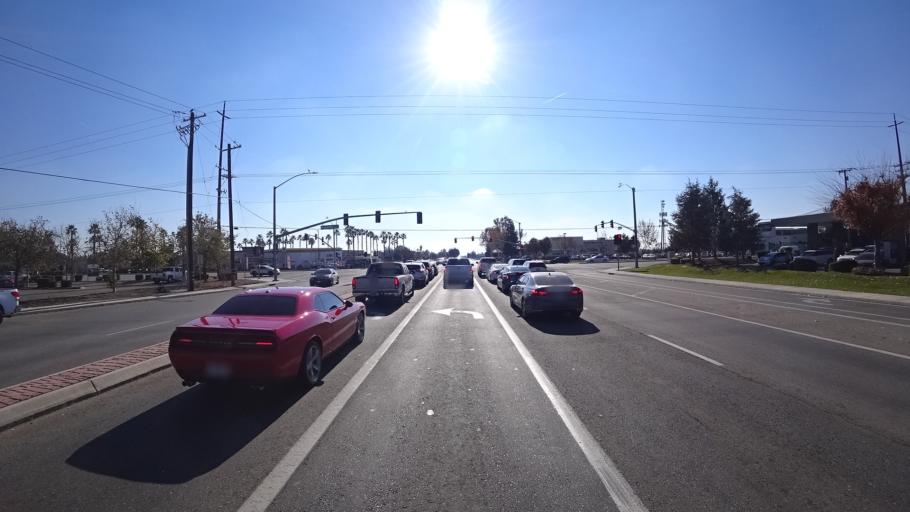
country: US
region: California
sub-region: Kern County
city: Greenfield
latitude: 35.2965
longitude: -119.0567
